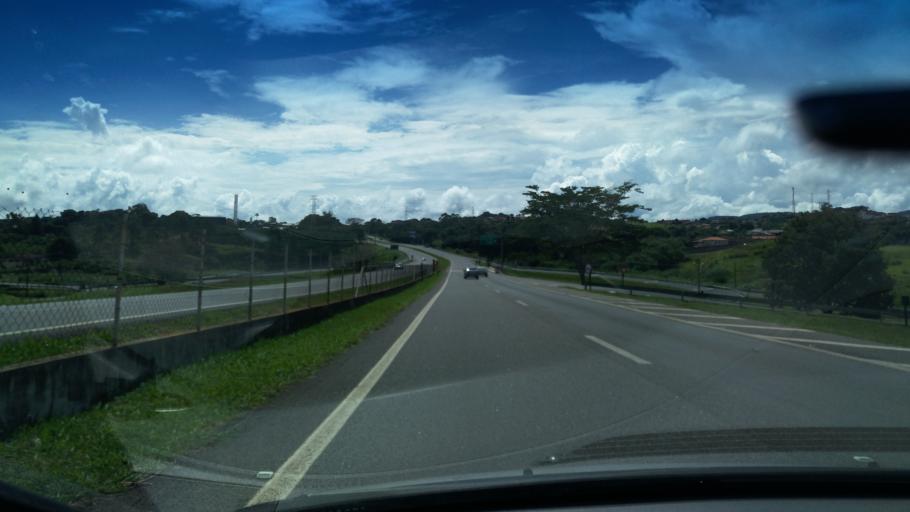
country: BR
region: Sao Paulo
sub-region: Santo Antonio Do Jardim
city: Espirito Santo do Pinhal
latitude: -22.1921
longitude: -46.7700
